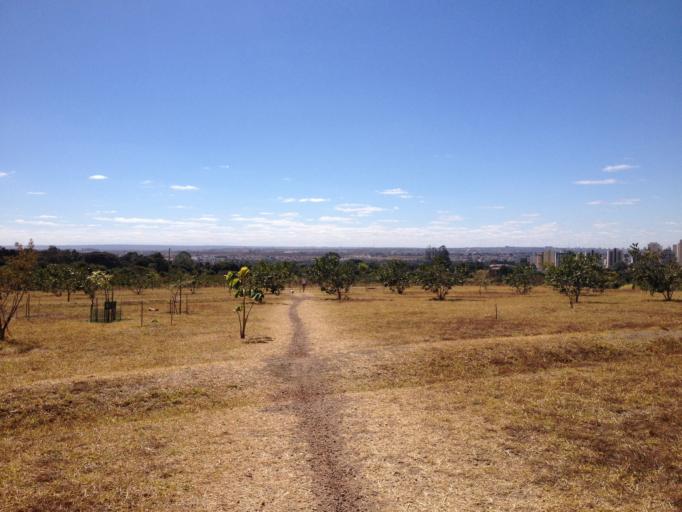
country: BR
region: Federal District
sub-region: Brasilia
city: Brasilia
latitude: -15.8343
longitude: -48.0299
